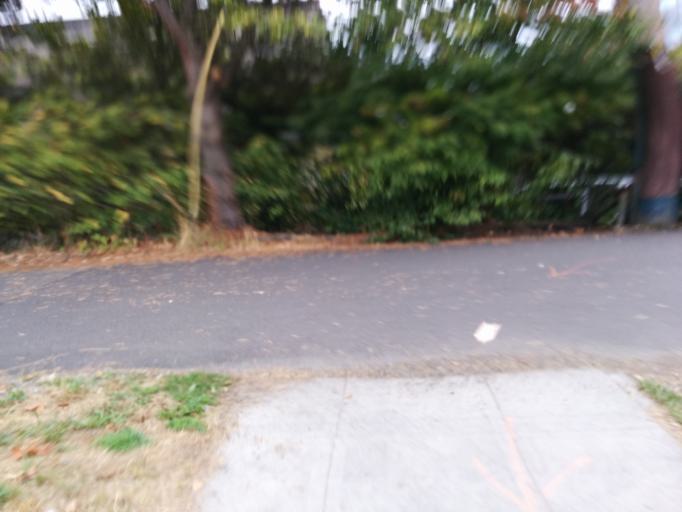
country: US
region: Washington
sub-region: King County
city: Seattle
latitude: 47.6556
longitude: -122.3207
